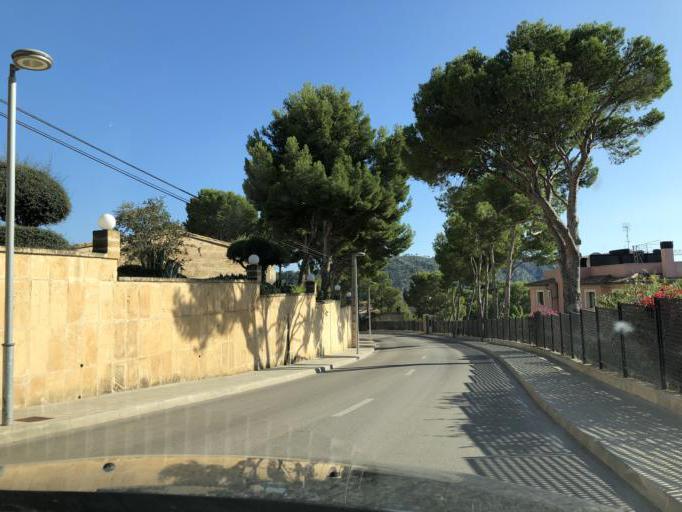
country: ES
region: Balearic Islands
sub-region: Illes Balears
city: Camp de Mar
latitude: 39.5417
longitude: 2.4144
